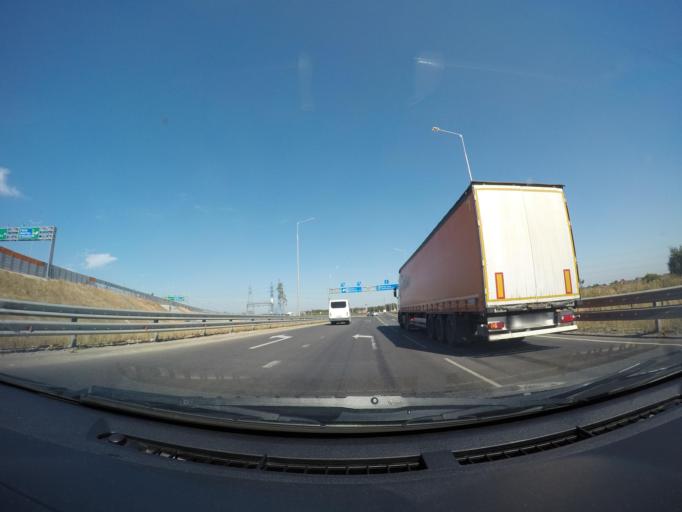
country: RU
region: Moskovskaya
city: Gzhel'
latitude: 55.6329
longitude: 38.3633
